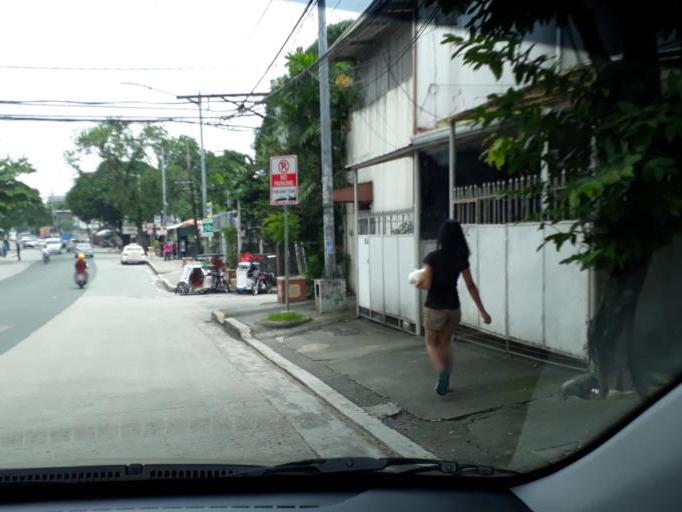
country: PH
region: Metro Manila
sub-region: Quezon City
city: Quezon City
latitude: 14.6313
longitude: 121.0549
